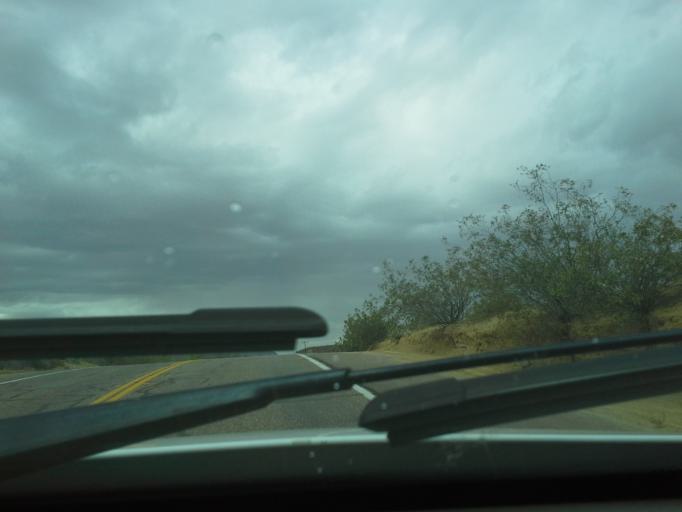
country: US
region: Arizona
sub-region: Pinal County
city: Apache Junction
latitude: 33.5501
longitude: -111.5833
